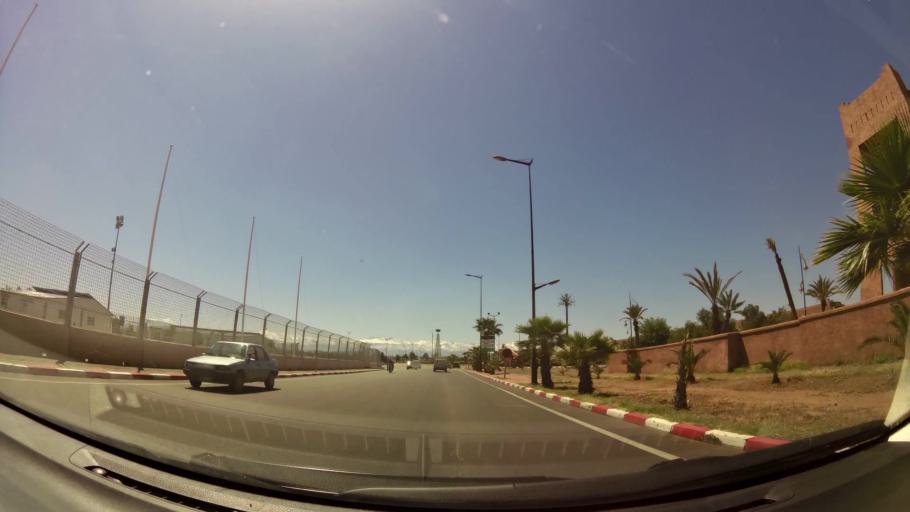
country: MA
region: Marrakech-Tensift-Al Haouz
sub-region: Marrakech
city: Marrakesh
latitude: 31.5800
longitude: -7.9826
